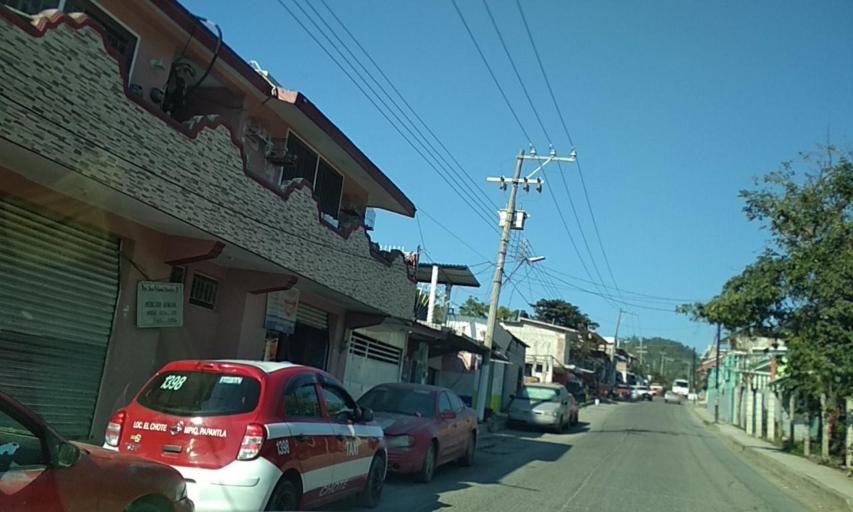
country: MX
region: Veracruz
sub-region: Papantla
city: El Chote
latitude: 20.4040
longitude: -97.3390
